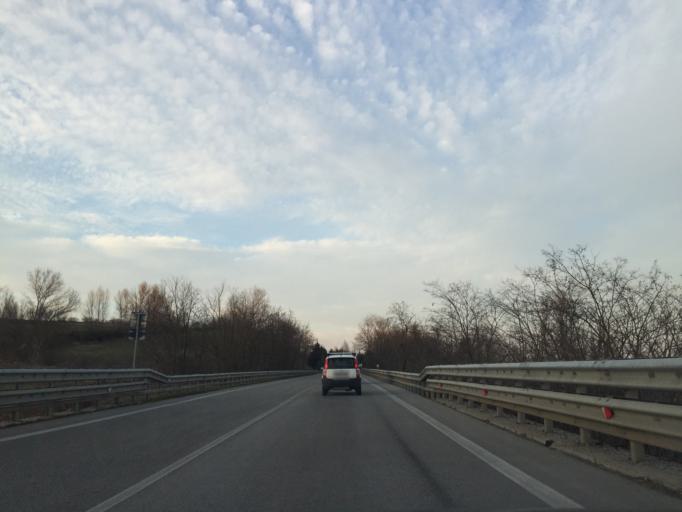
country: IT
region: Molise
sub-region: Provincia di Campobasso
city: Vinchiaturo
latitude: 41.5222
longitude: 14.6131
